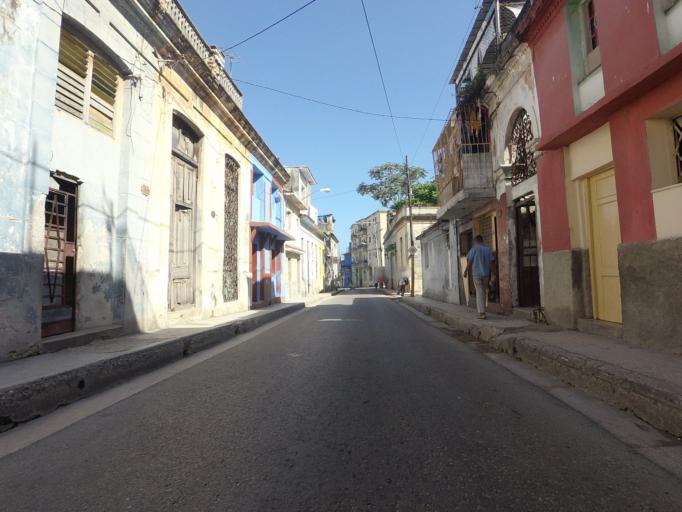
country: CU
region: La Habana
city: Cerro
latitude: 23.1186
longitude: -82.3731
